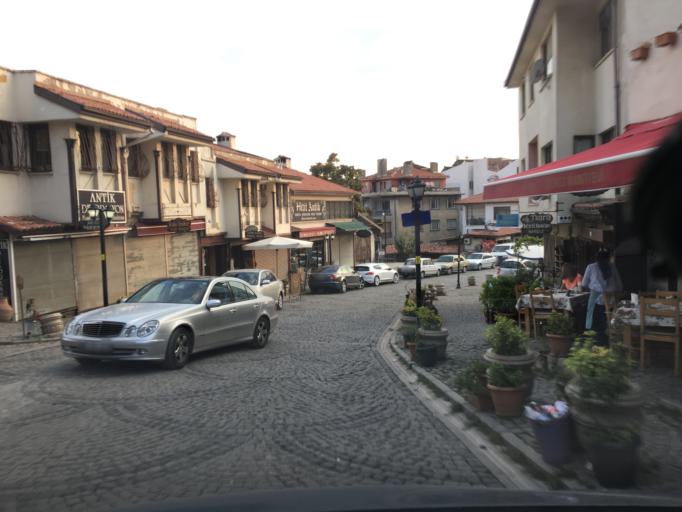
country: TR
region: Ankara
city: Cankaya
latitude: 39.9365
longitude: 32.8649
